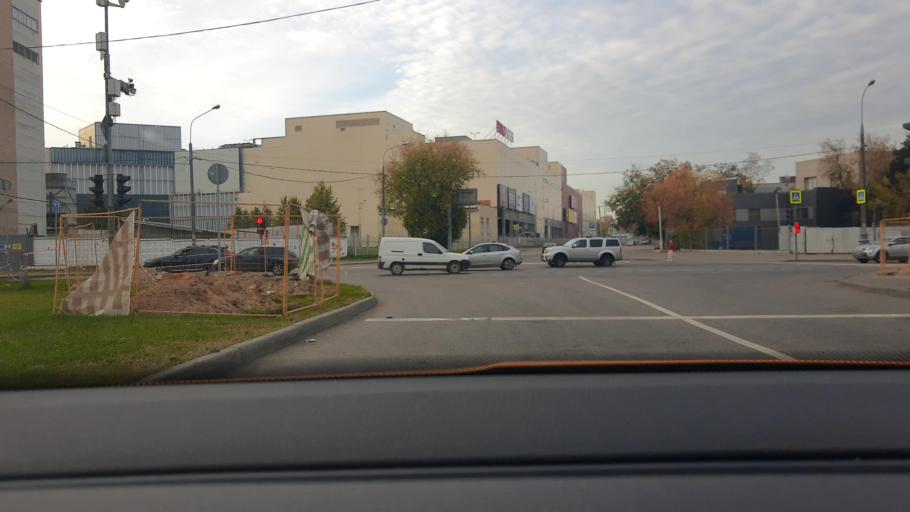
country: RU
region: Moscow
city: Leonovo
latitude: 55.8479
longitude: 37.6597
